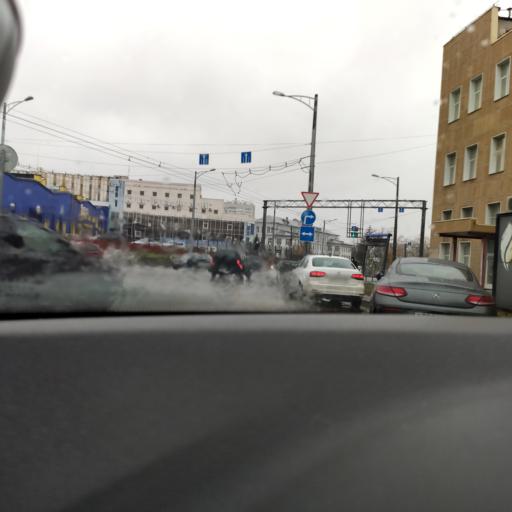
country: RU
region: Samara
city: Samara
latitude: 53.2036
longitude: 50.1515
